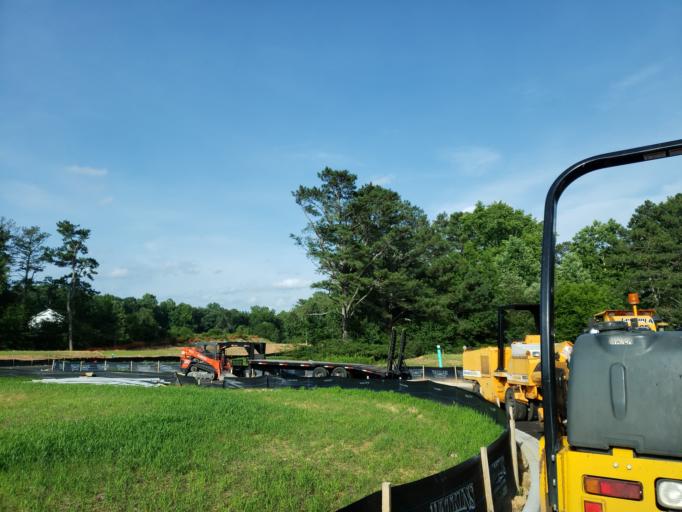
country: US
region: Georgia
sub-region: Cobb County
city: Powder Springs
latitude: 33.9083
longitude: -84.7057
